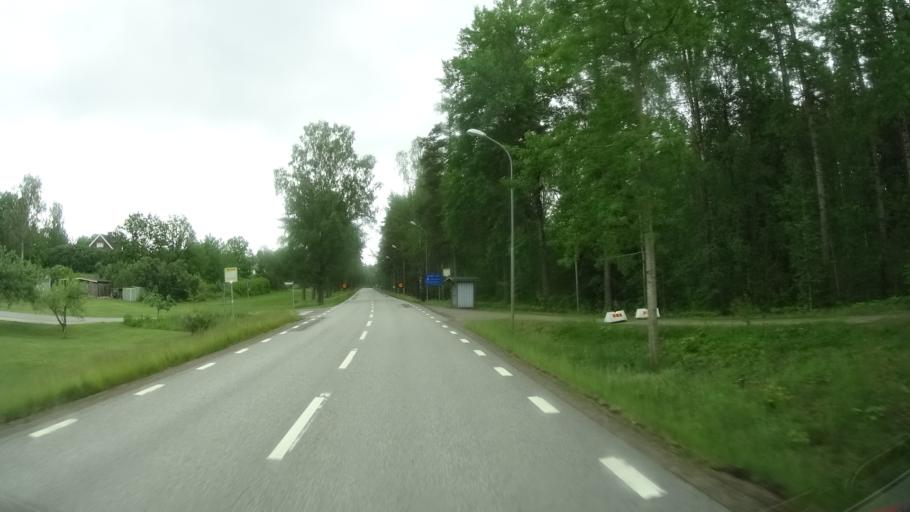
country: SE
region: Kalmar
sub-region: Hultsfreds Kommun
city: Hultsfred
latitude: 57.5350
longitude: 15.7642
